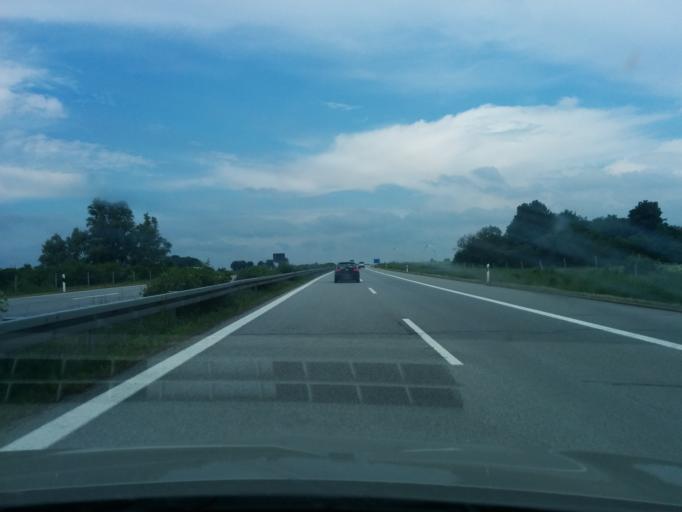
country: DE
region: Mecklenburg-Vorpommern
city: Burow
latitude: 53.7954
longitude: 13.3225
